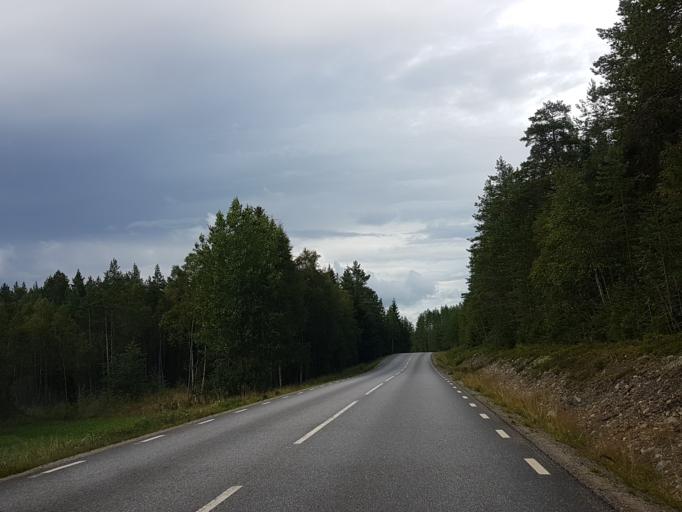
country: SE
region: Vaesterbotten
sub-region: Umea Kommun
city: Holmsund
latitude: 63.7702
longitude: 20.3871
